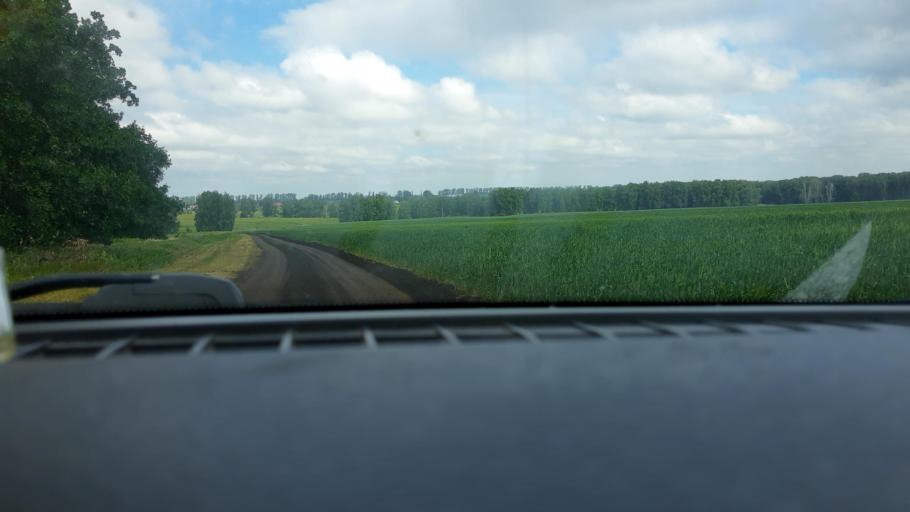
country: RU
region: Bashkortostan
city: Dmitriyevka
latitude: 54.7112
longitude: 55.4945
